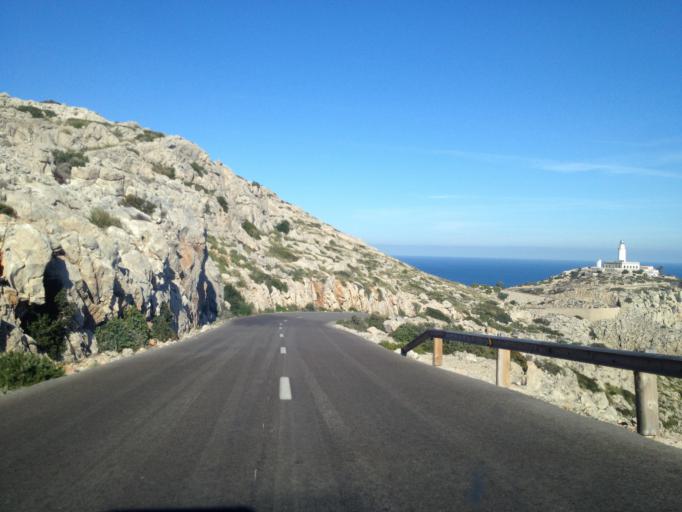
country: ES
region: Balearic Islands
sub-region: Illes Balears
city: Alcudia
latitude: 39.9557
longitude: 3.2118
